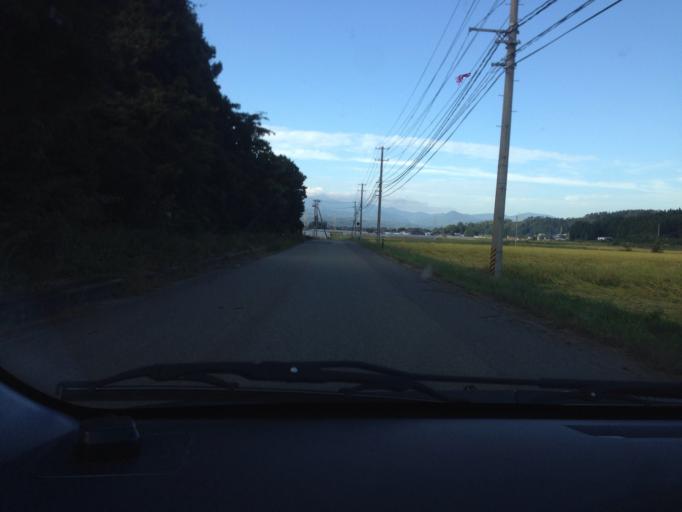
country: JP
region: Fukushima
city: Kitakata
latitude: 37.5843
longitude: 139.7701
